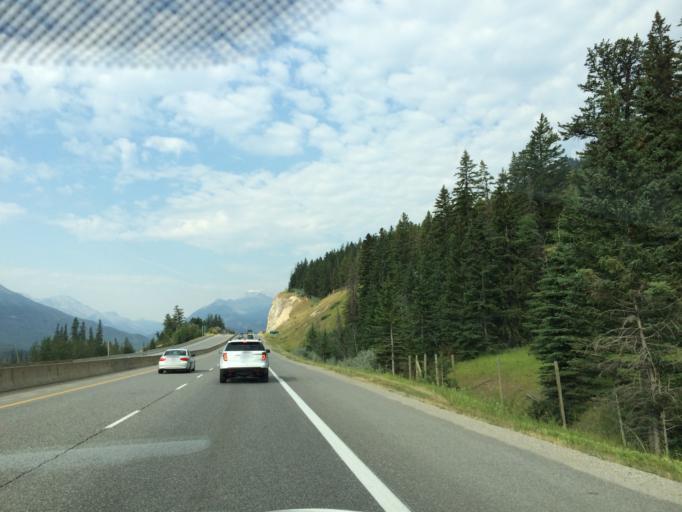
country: CA
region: Alberta
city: Banff
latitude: 51.1866
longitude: -115.5885
